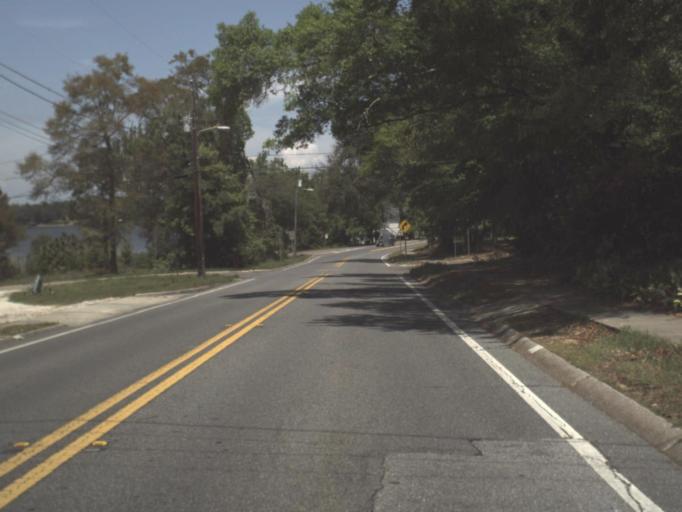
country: US
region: Florida
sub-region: Escambia County
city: East Pensacola Heights
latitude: 30.4307
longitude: -87.1830
